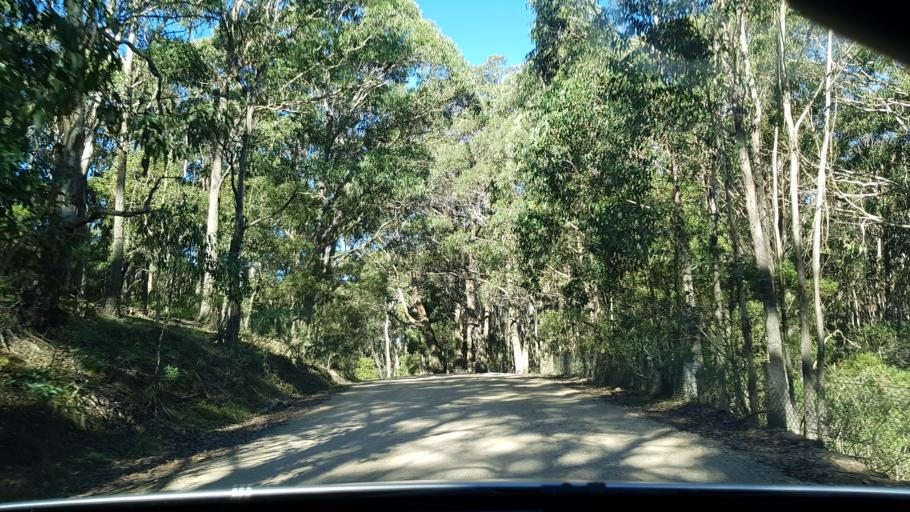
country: AU
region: New South Wales
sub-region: Oberon
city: Oberon
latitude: -33.8536
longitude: 150.0315
